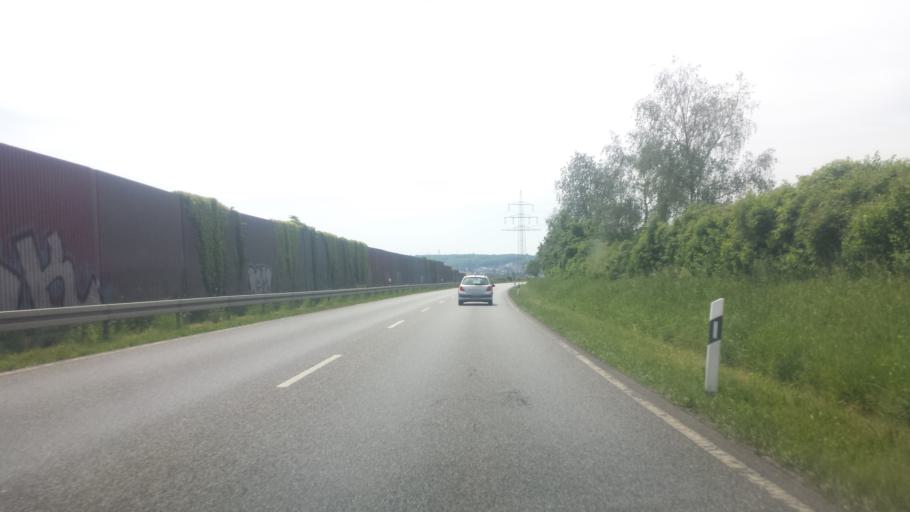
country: DE
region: Hesse
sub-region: Regierungsbezirk Darmstadt
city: Bad Vilbel
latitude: 50.2033
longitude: 8.7364
